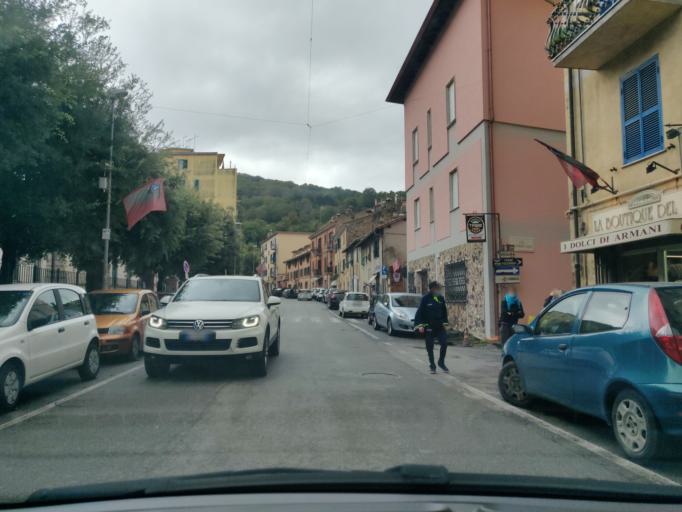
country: IT
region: Latium
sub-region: Citta metropolitana di Roma Capitale
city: Allumiere
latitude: 42.1555
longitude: 11.9044
